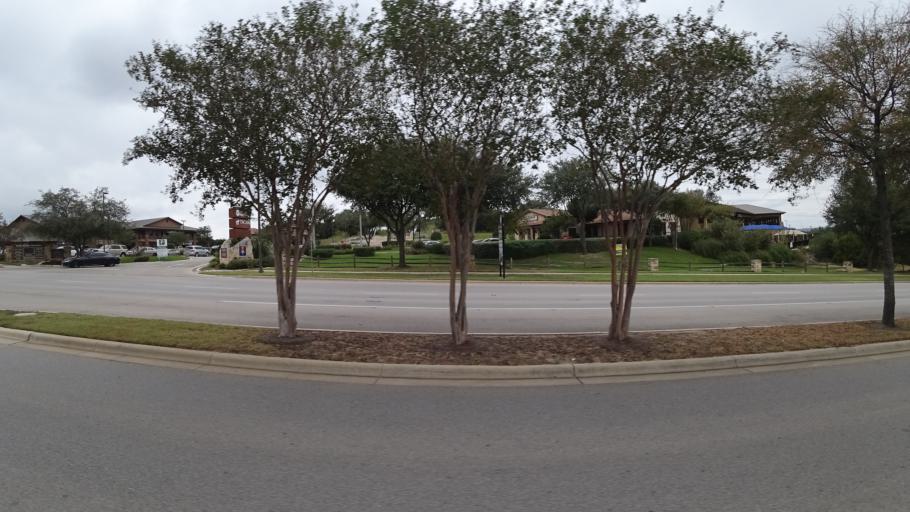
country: US
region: Texas
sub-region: Travis County
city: Hudson Bend
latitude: 30.3822
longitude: -97.8839
